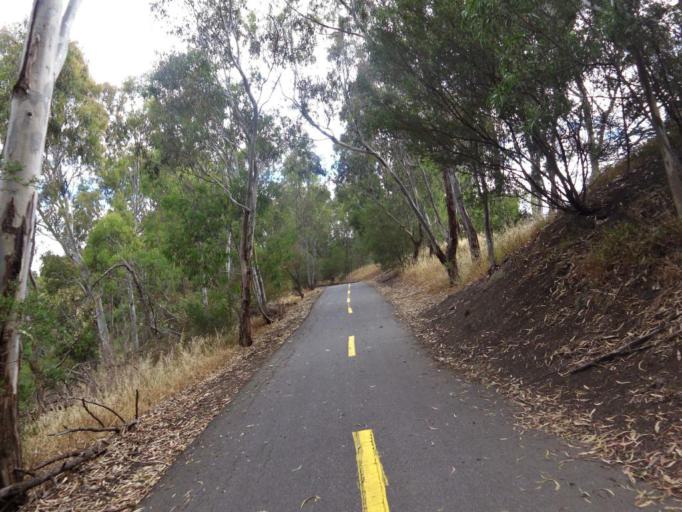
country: AU
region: Victoria
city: Heidelberg West
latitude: -37.7533
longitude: 145.0318
